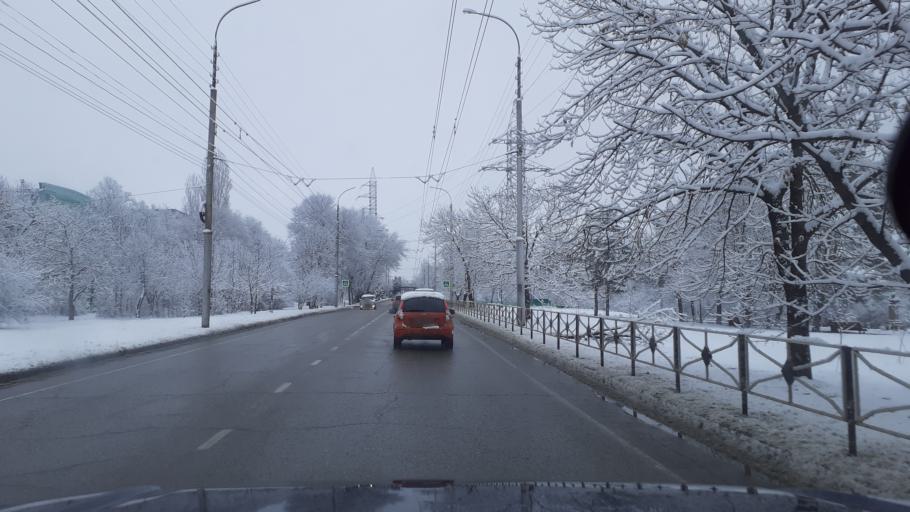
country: RU
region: Adygeya
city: Maykop
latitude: 44.5912
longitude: 40.1160
